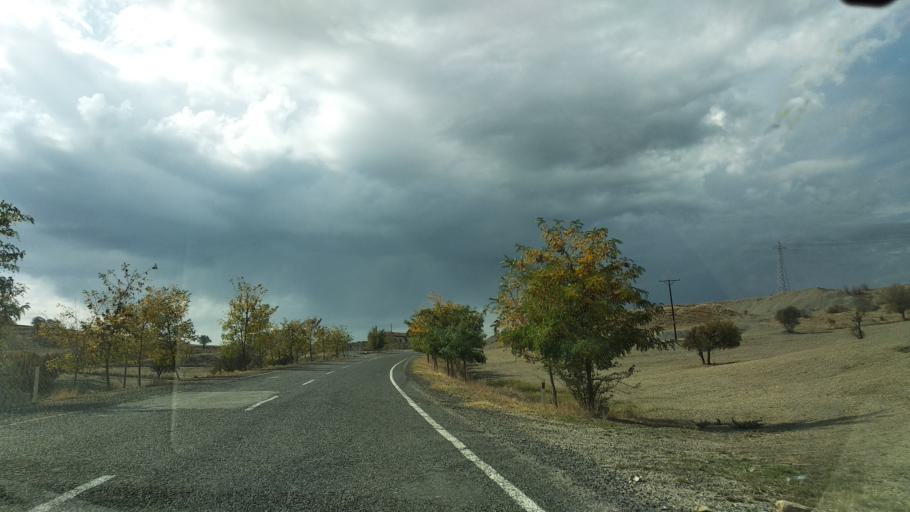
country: TR
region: Bolu
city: Seben
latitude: 40.3791
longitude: 31.5226
